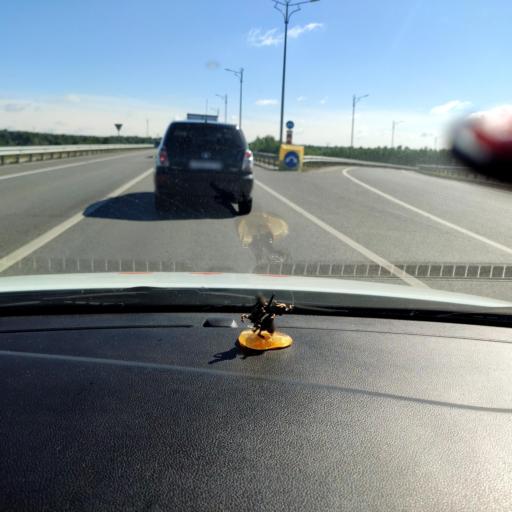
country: RU
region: Tatarstan
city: Stolbishchi
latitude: 55.6981
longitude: 49.2238
